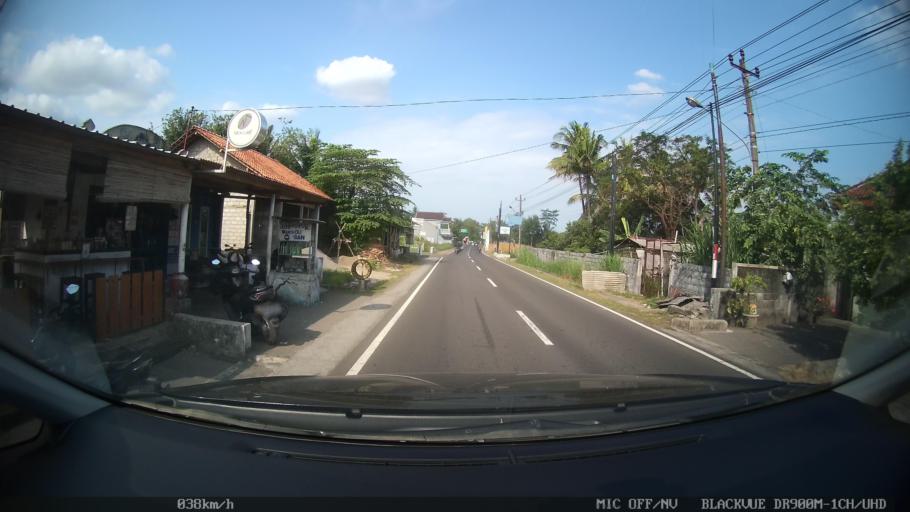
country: ID
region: Central Java
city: Candi Prambanan
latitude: -7.7287
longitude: 110.4699
